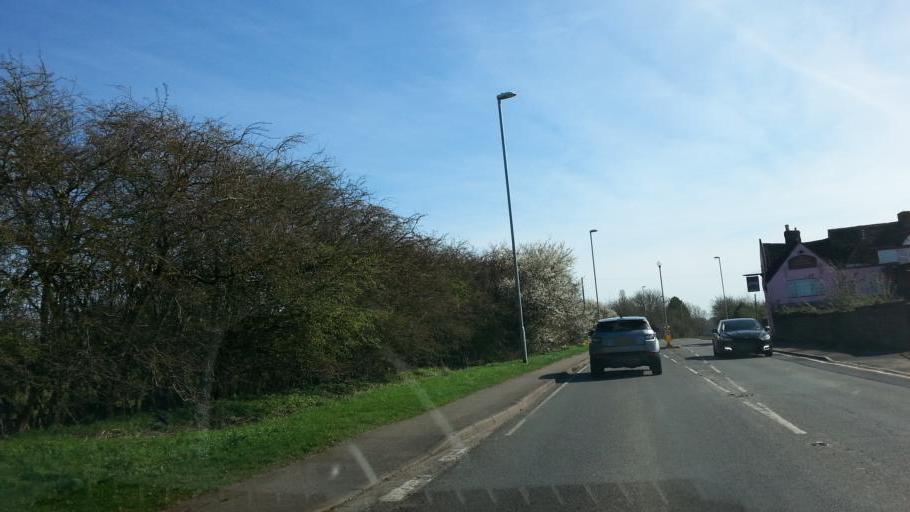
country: GB
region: England
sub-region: Cambridgeshire
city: Great Stukeley
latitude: 52.3584
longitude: -0.2142
